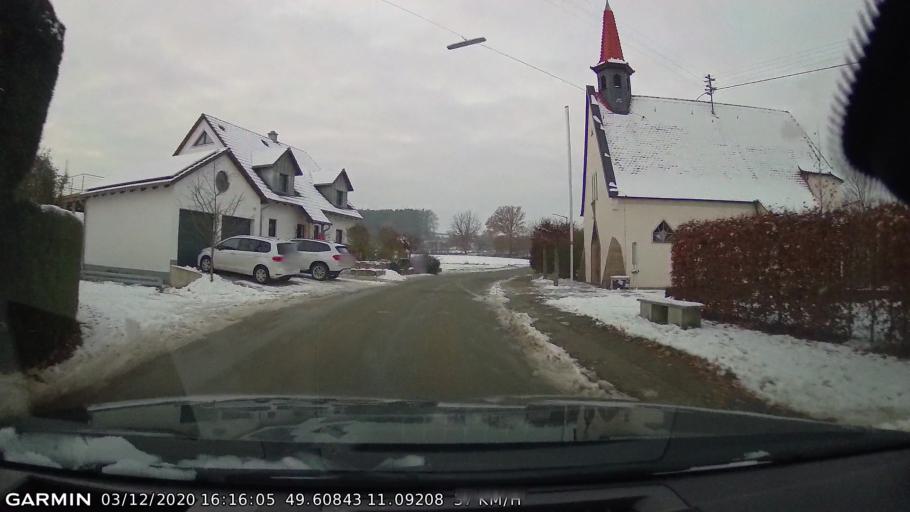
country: DE
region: Bavaria
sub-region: Regierungsbezirk Mittelfranken
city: Uttenreuth
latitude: 49.6084
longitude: 11.0920
